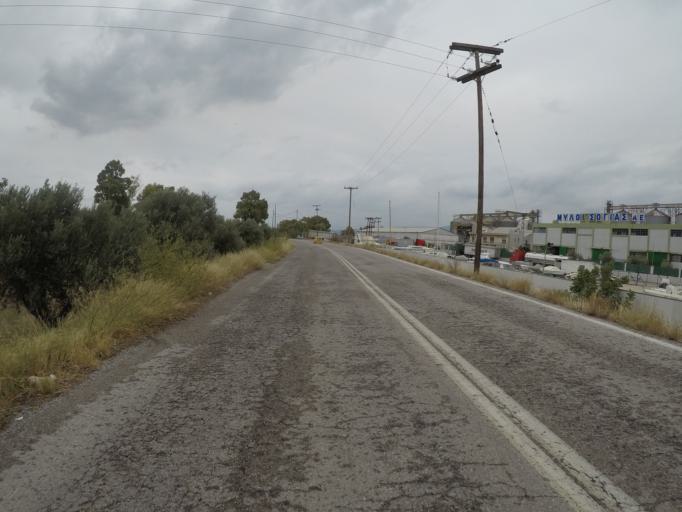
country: GR
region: Peloponnese
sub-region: Nomos Korinthias
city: Isthmia
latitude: 37.9223
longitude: 23.0226
